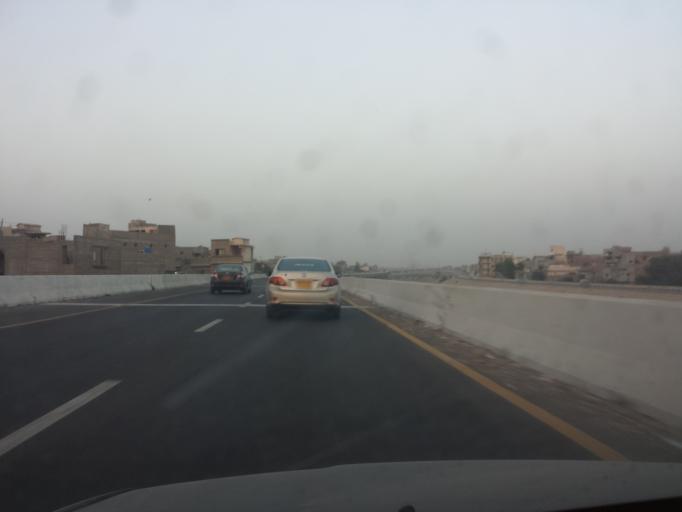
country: PK
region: Sindh
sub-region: Karachi District
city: Karachi
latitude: 24.8960
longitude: 67.0495
